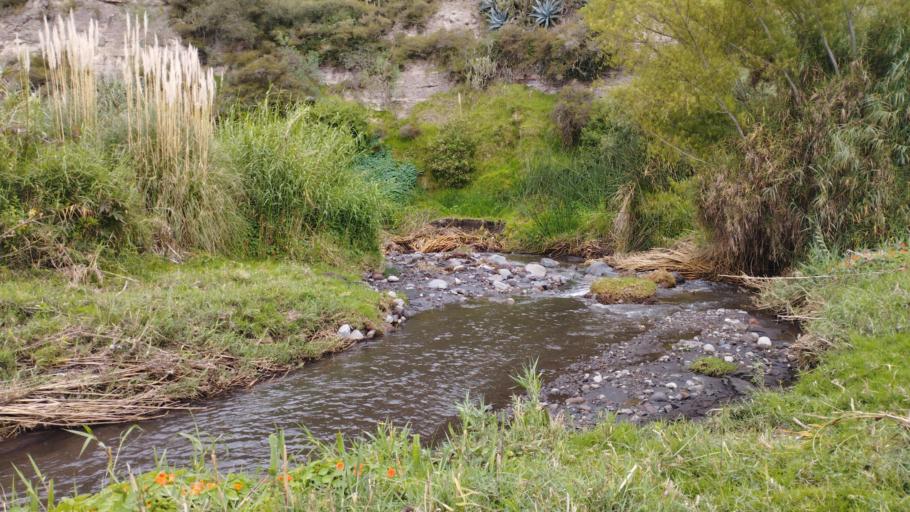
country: EC
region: Chimborazo
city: Guano
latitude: -1.6149
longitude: -78.6092
